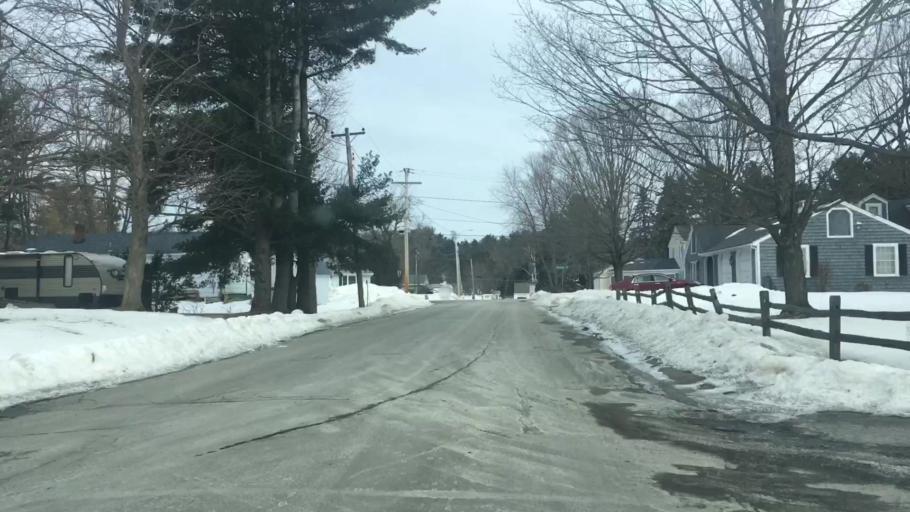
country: US
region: Maine
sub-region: Kennebec County
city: Augusta
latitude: 44.3070
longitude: -69.7577
